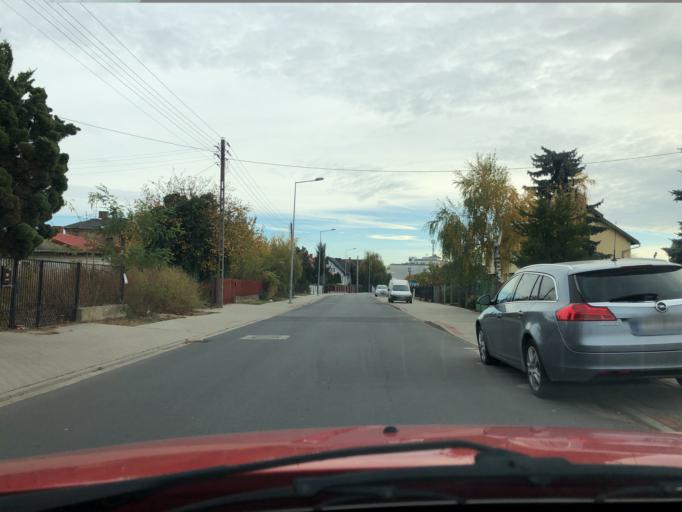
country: PL
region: Greater Poland Voivodeship
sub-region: Powiat poznanski
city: Plewiska
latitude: 52.3834
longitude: 16.8480
